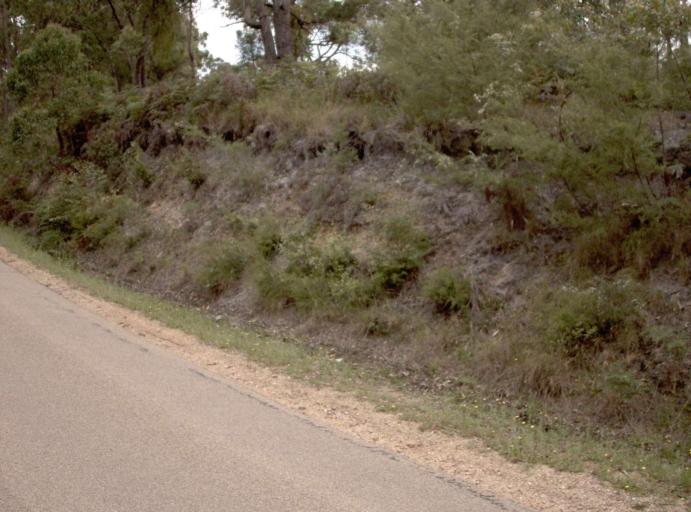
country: AU
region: Victoria
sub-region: East Gippsland
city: Bairnsdale
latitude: -37.7469
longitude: 147.5973
